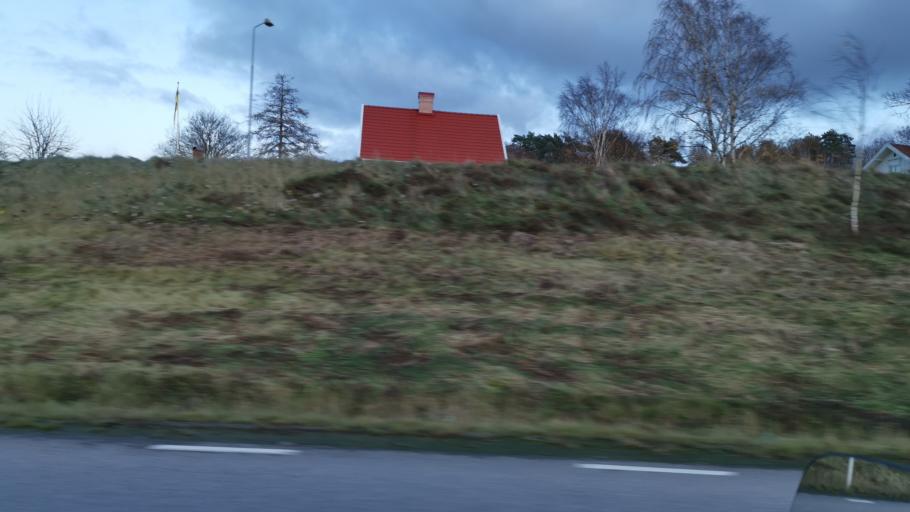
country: SE
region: Vaestra Goetaland
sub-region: Munkedals Kommun
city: Munkedal
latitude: 58.4632
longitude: 11.6571
